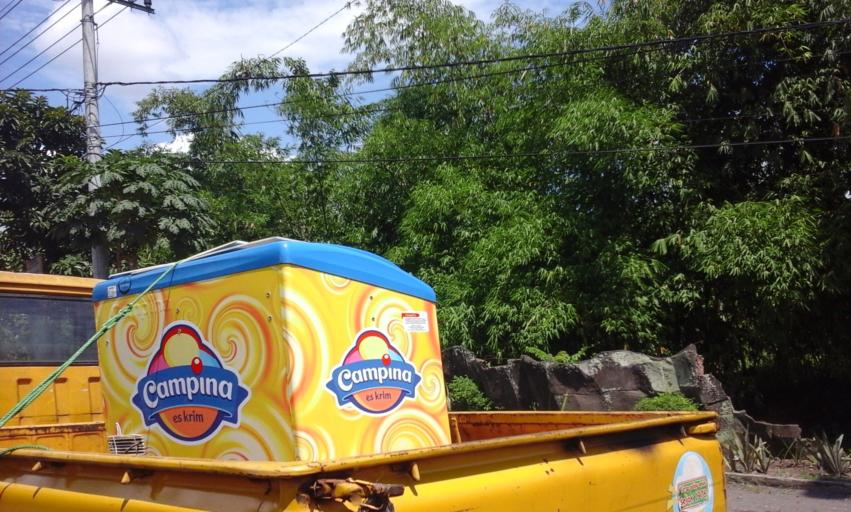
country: ID
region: East Java
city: Sumberketangi
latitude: -8.1875
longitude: 113.7472
